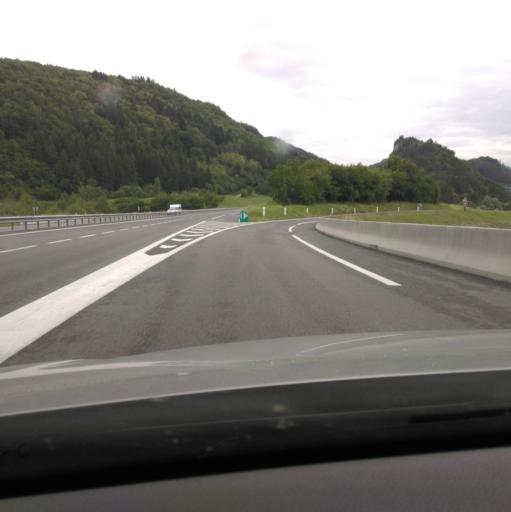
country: FR
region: Rhone-Alpes
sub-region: Departement de l'Ain
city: Montreal-la-Cluse
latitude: 46.1773
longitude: 5.5604
